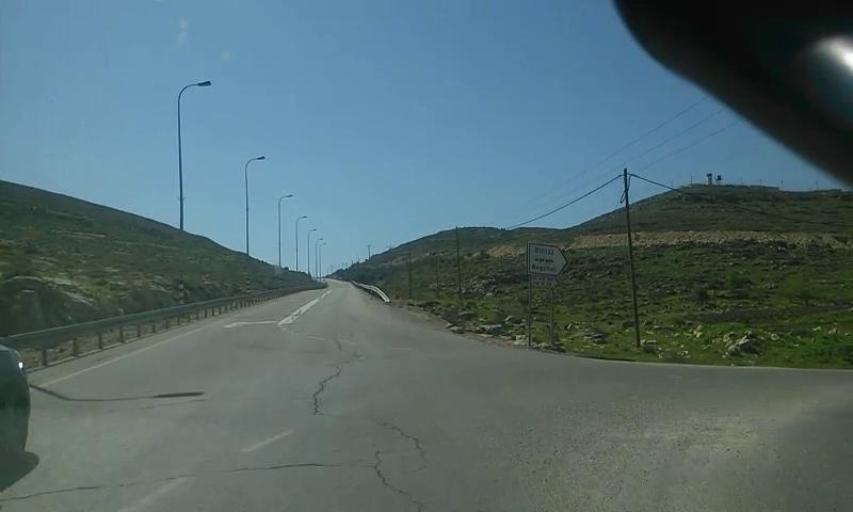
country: PS
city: Khursa
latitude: 31.4800
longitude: 35.0464
